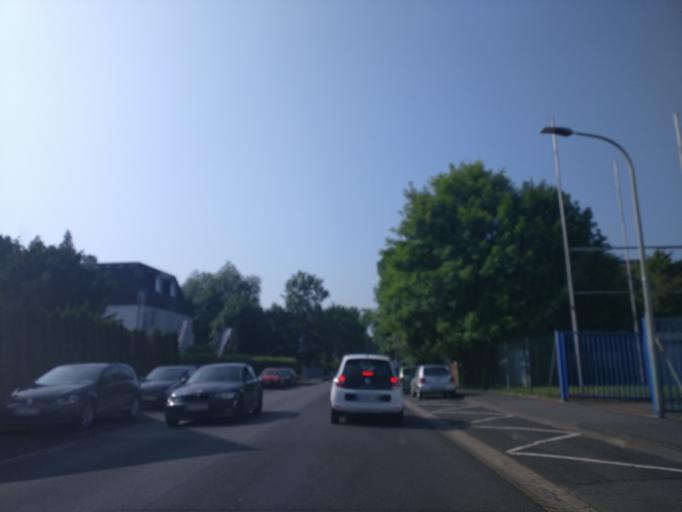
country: DE
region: Lower Saxony
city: Rosdorf
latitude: 51.5072
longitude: 9.9095
